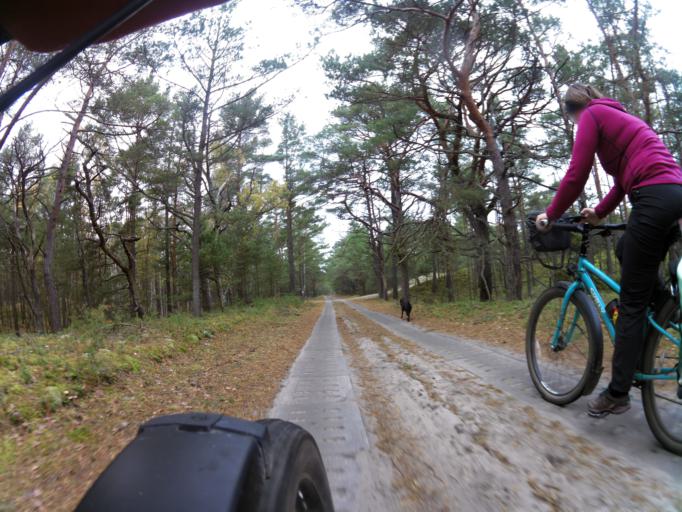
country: PL
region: Pomeranian Voivodeship
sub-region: Powiat pucki
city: Hel
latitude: 54.6293
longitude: 18.8122
